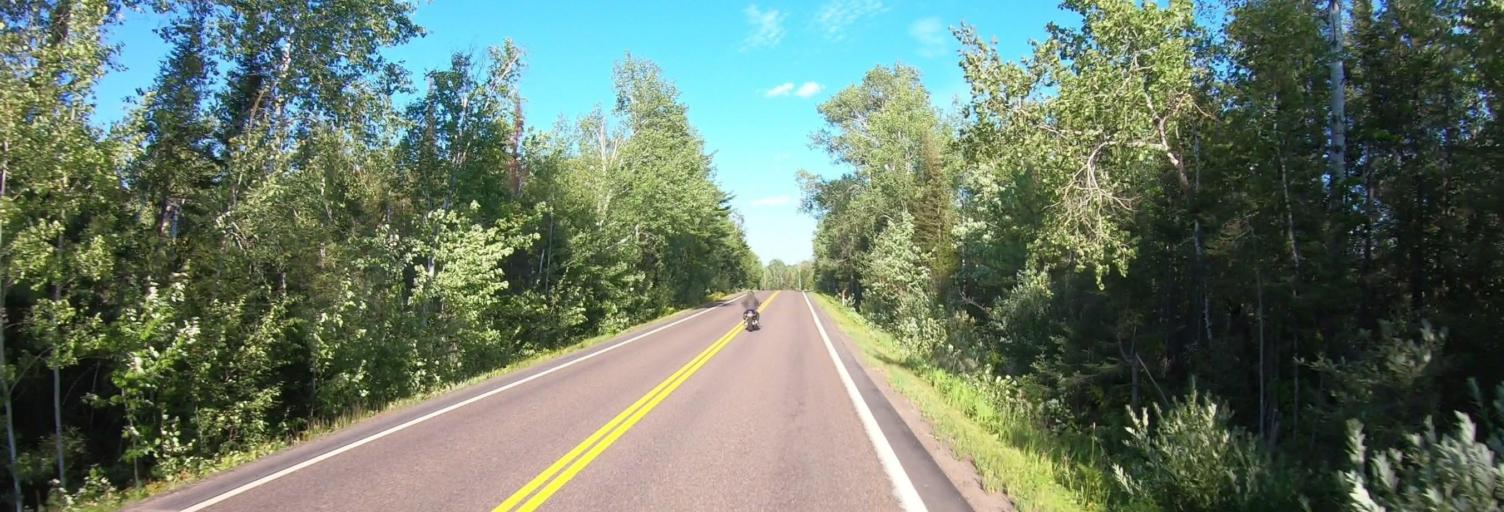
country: US
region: Minnesota
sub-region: Saint Louis County
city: Ely
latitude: 47.9597
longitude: -91.5765
